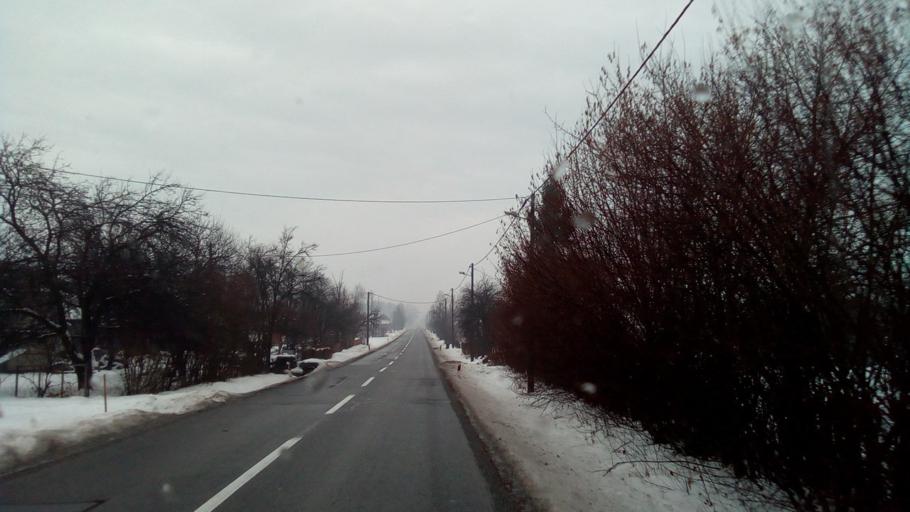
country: HR
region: Sisacko-Moslavacka
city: Petrinja
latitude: 45.4715
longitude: 16.2550
